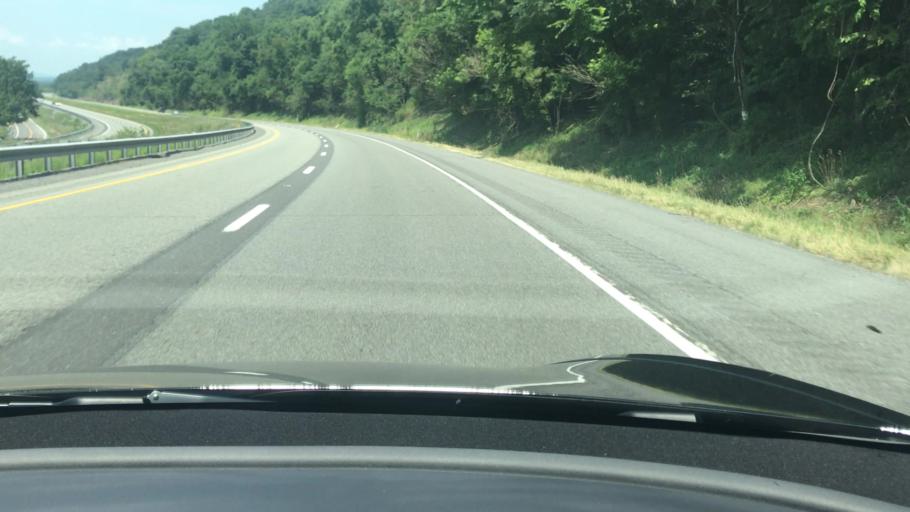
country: US
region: Pennsylvania
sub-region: Perry County
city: Newport
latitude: 40.5658
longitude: -77.1728
